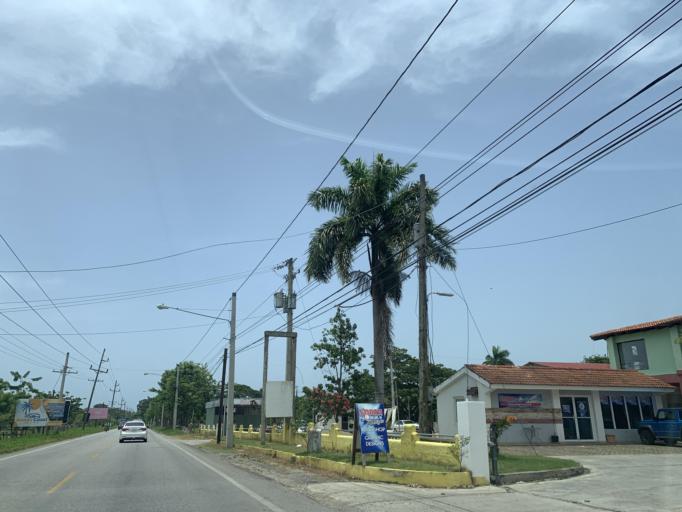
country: DO
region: Puerto Plata
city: Cabarete
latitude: 19.7751
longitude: -70.4914
